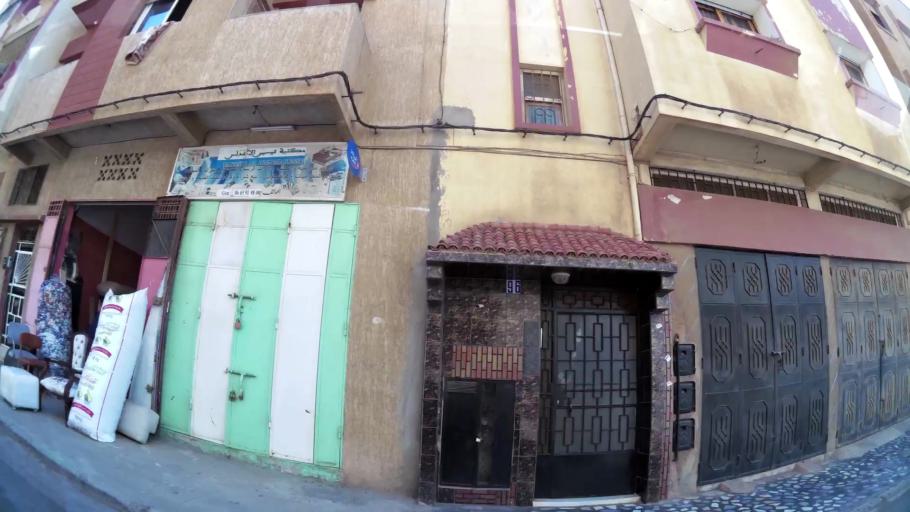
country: MA
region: Rabat-Sale-Zemmour-Zaer
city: Sale
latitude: 34.0472
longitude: -6.7878
